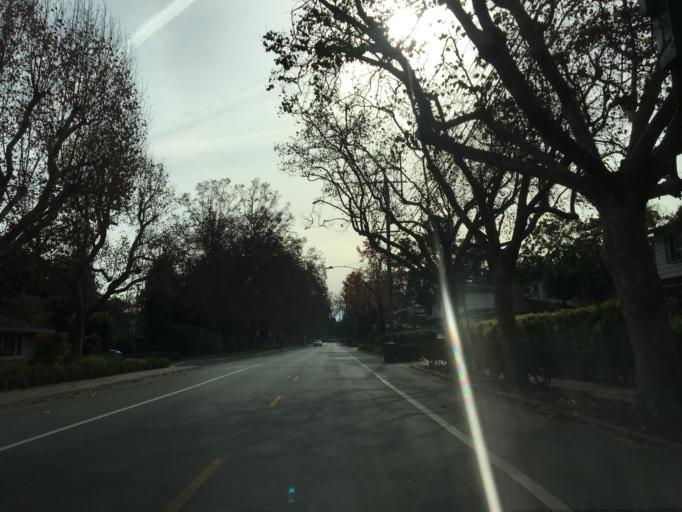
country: US
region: California
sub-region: Santa Clara County
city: Palo Alto
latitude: 37.4466
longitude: -122.1398
